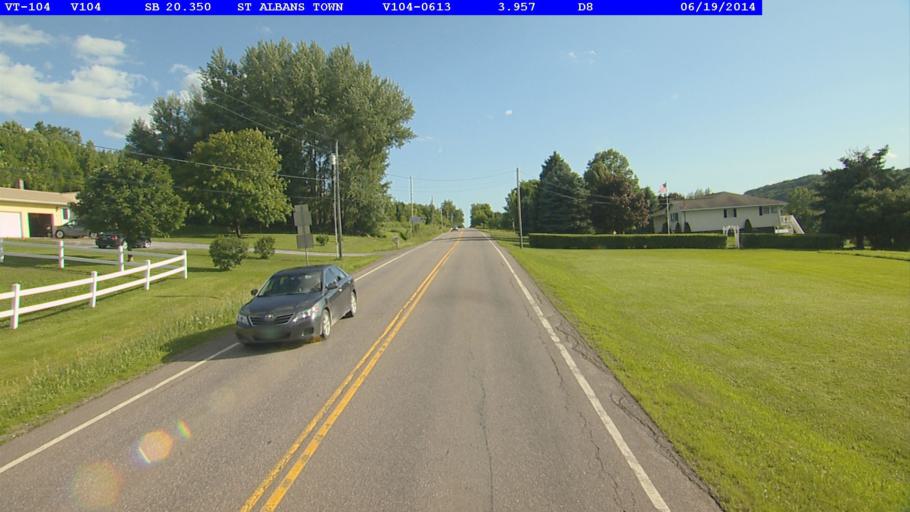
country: US
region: Vermont
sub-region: Franklin County
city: Saint Albans
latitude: 44.8268
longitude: -73.0549
